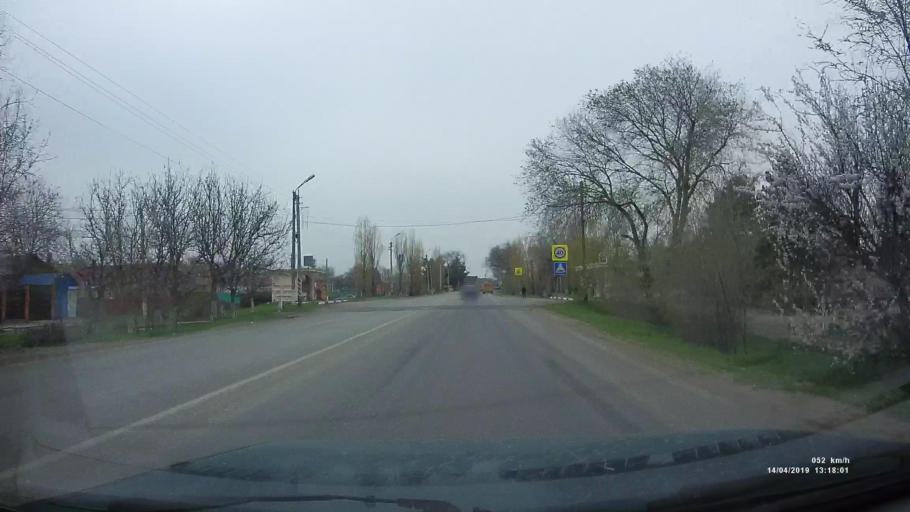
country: RU
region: Rostov
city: Kuleshovka
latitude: 47.0784
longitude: 39.5581
